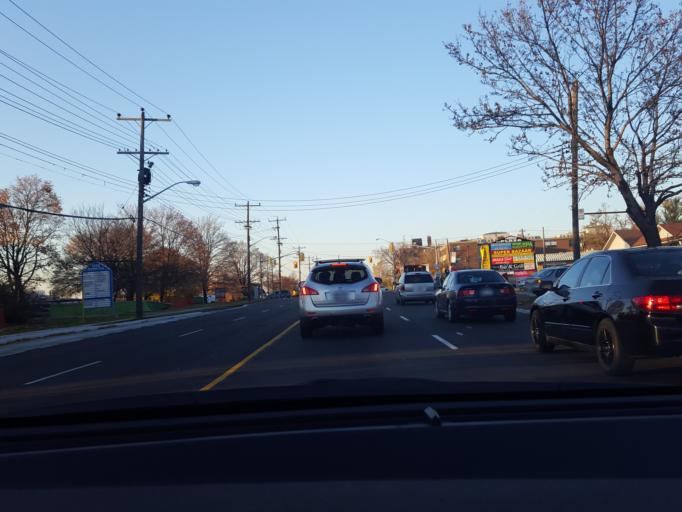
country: CA
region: Ontario
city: Scarborough
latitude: 43.7581
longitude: -79.2892
